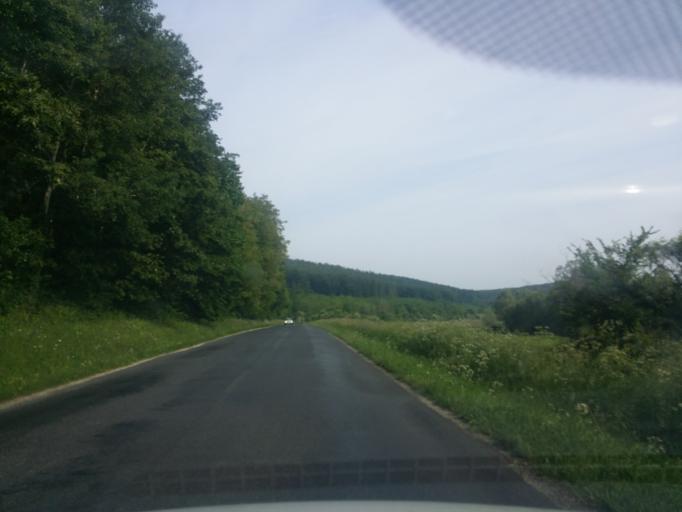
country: HU
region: Zala
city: Heviz
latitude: 46.8718
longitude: 17.1513
